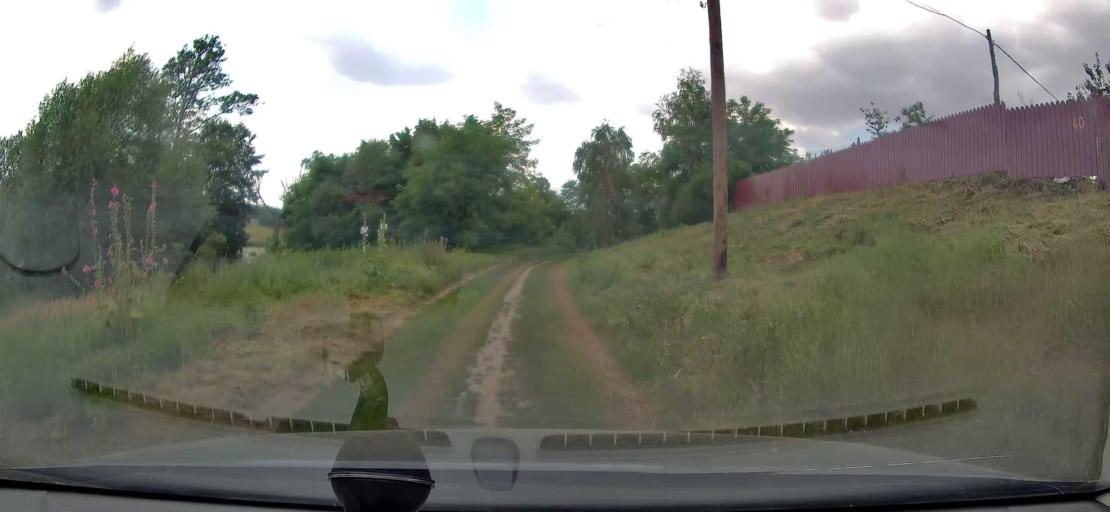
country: RU
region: Kursk
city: Zolotukhino
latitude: 52.0301
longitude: 36.1997
